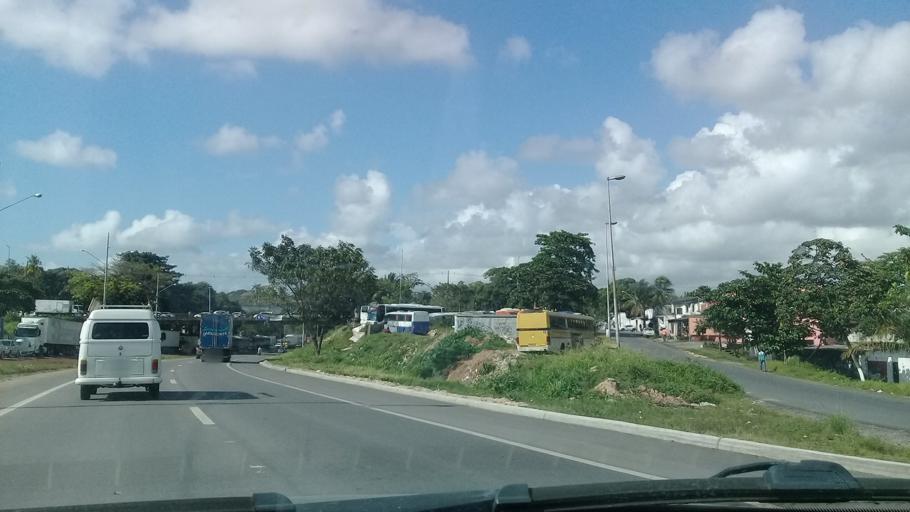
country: BR
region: Pernambuco
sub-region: Jaboatao Dos Guararapes
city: Jaboatao dos Guararapes
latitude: -8.0908
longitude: -34.9469
